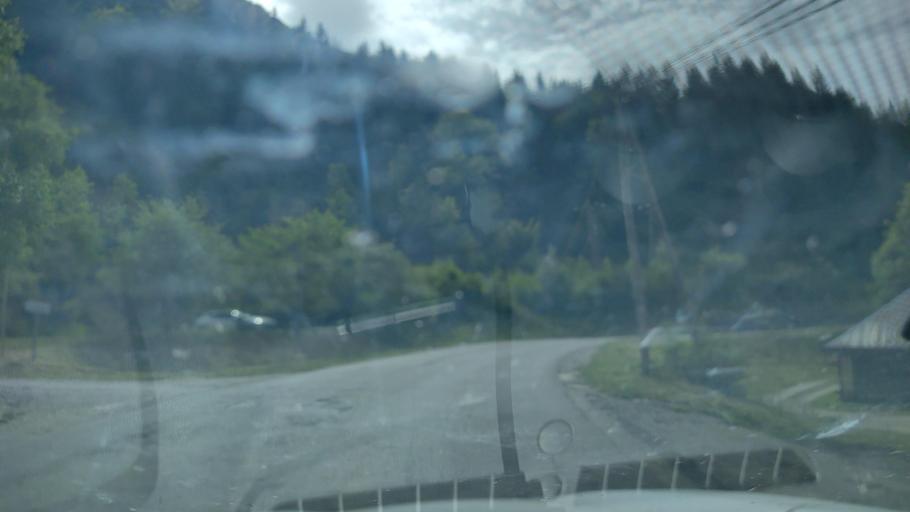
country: FR
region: Rhone-Alpes
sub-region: Departement de la Savoie
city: Cruet
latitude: 45.6166
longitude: 6.0865
